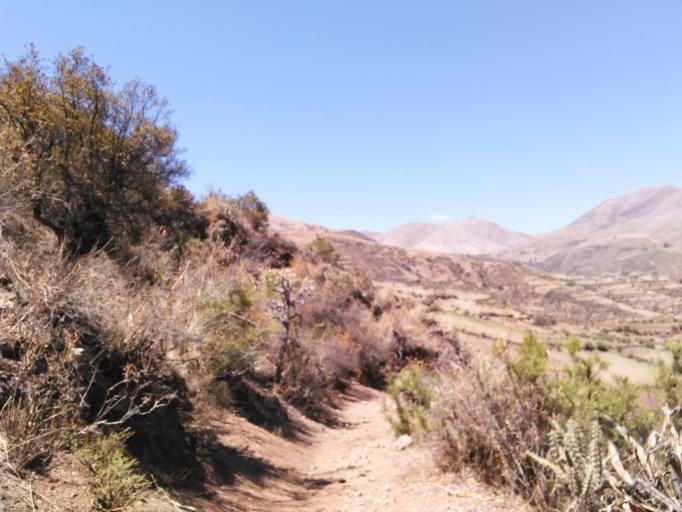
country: PE
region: Ayacucho
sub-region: Provincia de Victor Fajardo
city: Canaria
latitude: -13.8828
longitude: -73.9501
